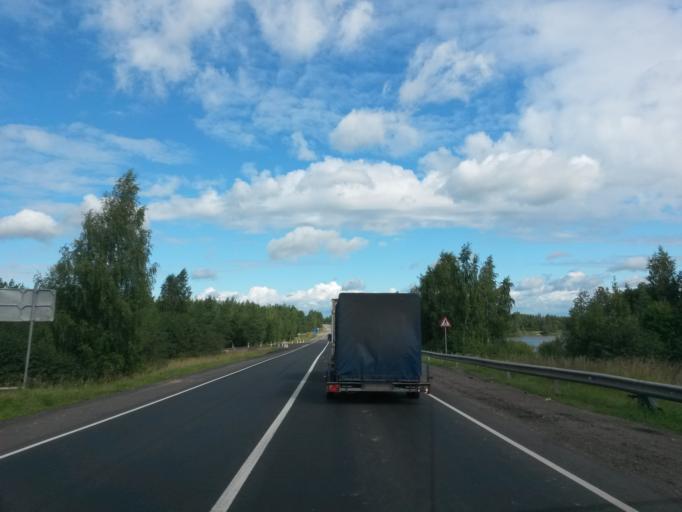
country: RU
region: Jaroslavl
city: Yaroslavl
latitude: 57.5071
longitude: 39.8980
